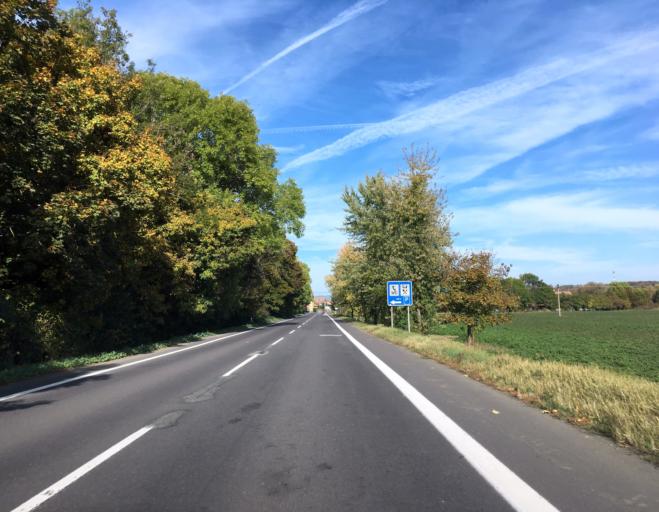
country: SK
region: Banskobystricky
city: Dudince
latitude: 48.1491
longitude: 18.8715
